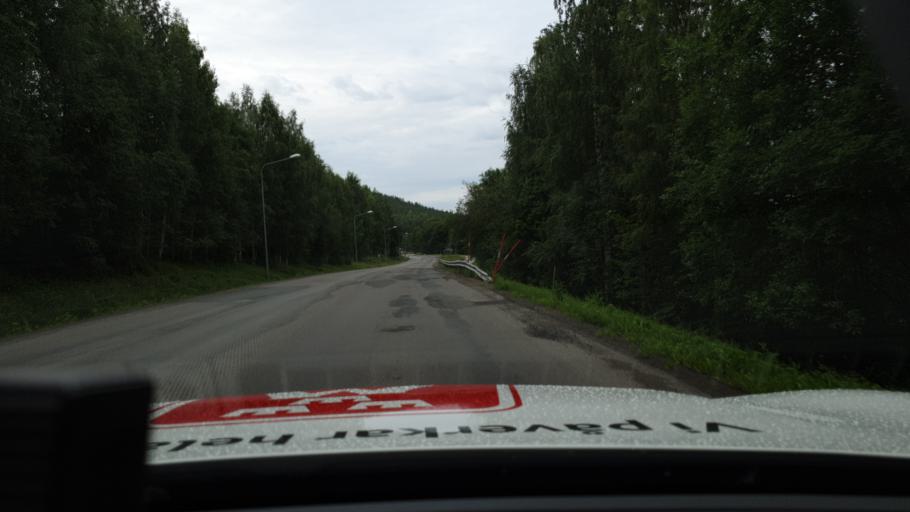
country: SE
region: Norrbotten
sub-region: Bodens Kommun
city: Boden
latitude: 65.8411
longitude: 21.6061
